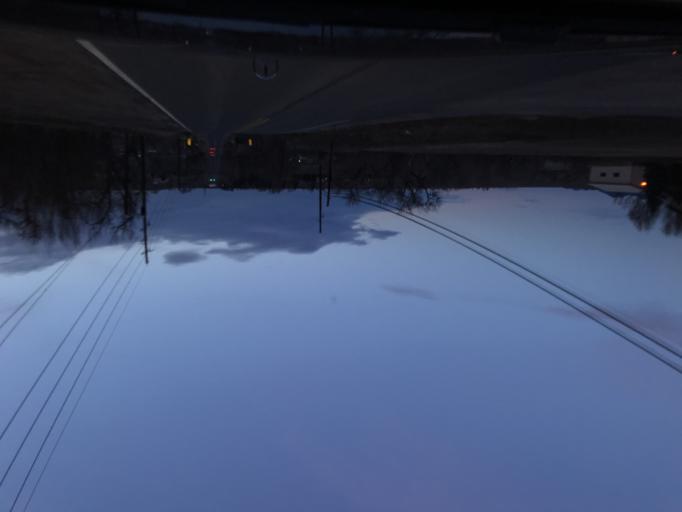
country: US
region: Colorado
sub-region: Jefferson County
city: Applewood
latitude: 39.8363
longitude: -105.1651
